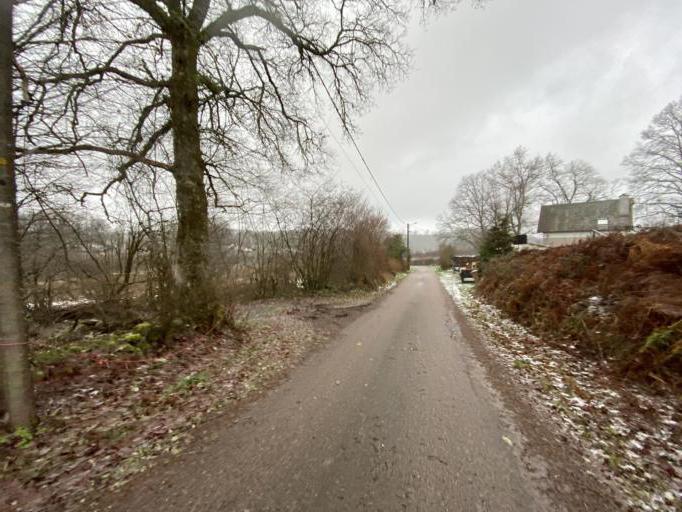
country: FR
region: Bourgogne
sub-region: Departement de la Cote-d'Or
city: Saulieu
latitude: 47.2680
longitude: 4.1560
